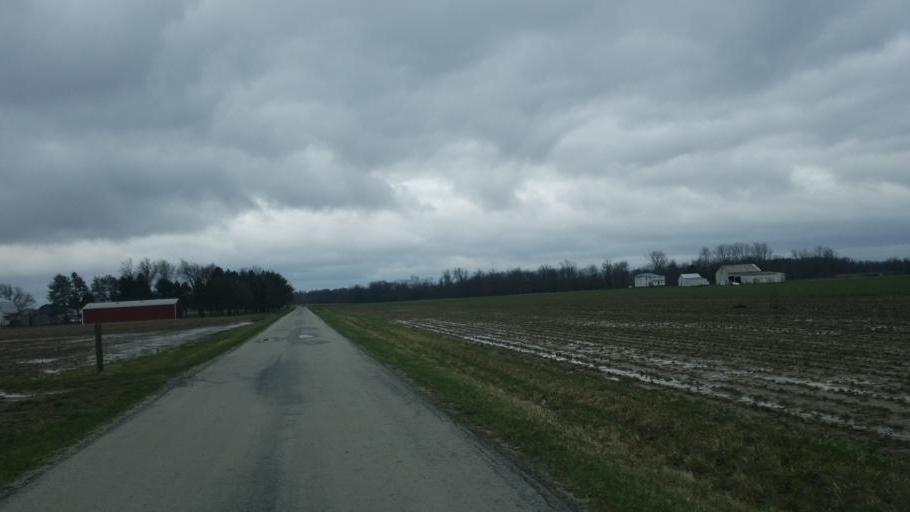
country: US
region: Ohio
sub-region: Hardin County
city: Forest
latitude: 40.7275
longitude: -83.4601
